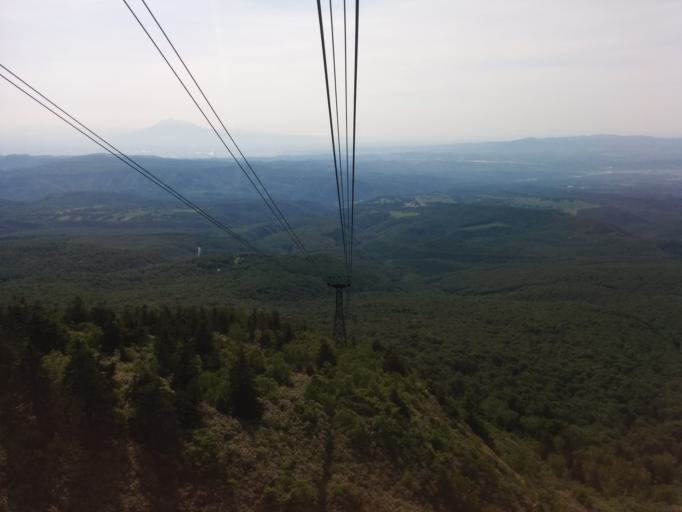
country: JP
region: Aomori
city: Aomori Shi
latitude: 40.6764
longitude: 140.8562
